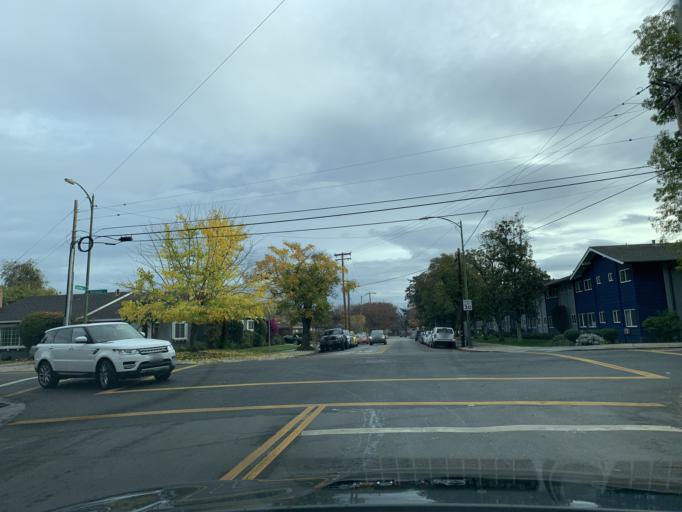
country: US
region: California
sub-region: Santa Clara County
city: Cambrian Park
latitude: 37.2474
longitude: -121.9506
